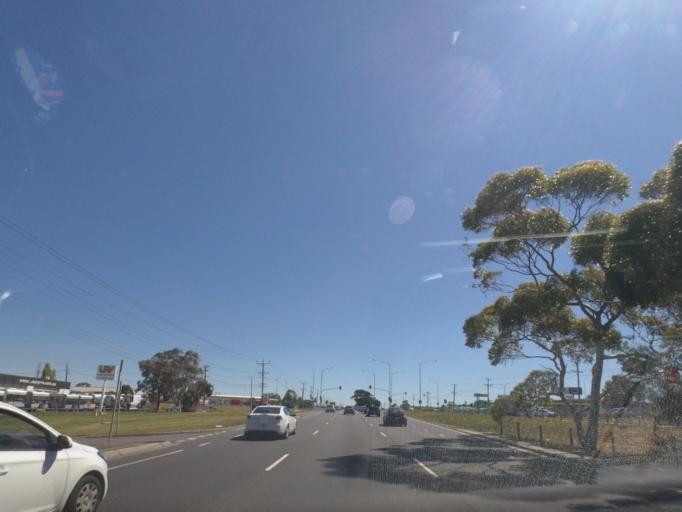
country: AU
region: Victoria
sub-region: Hume
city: Coolaroo
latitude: -37.6487
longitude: 144.9520
